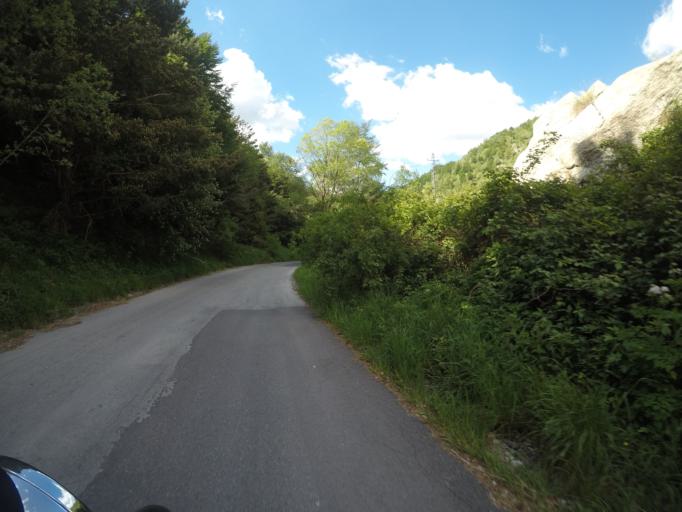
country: IT
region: Tuscany
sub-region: Provincia di Lucca
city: Minucciano
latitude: 44.1386
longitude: 10.1960
